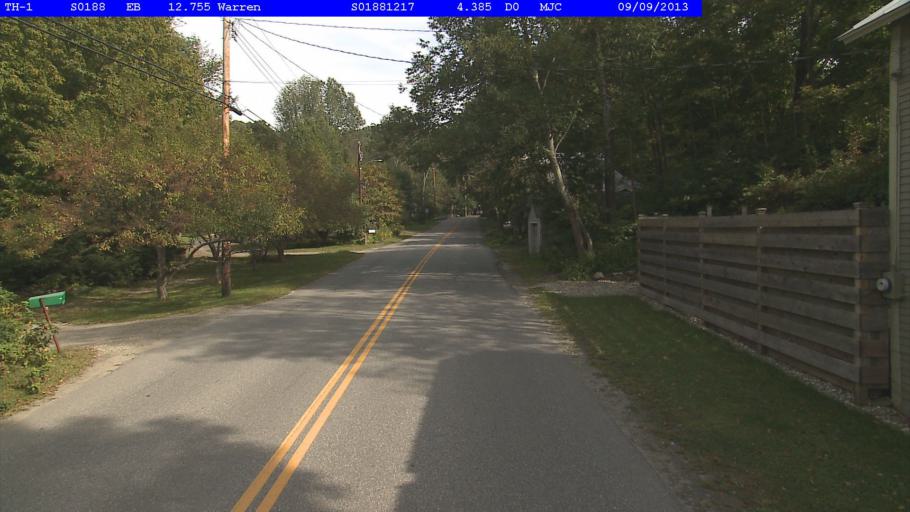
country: US
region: Vermont
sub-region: Washington County
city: Northfield
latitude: 44.1145
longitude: -72.8535
